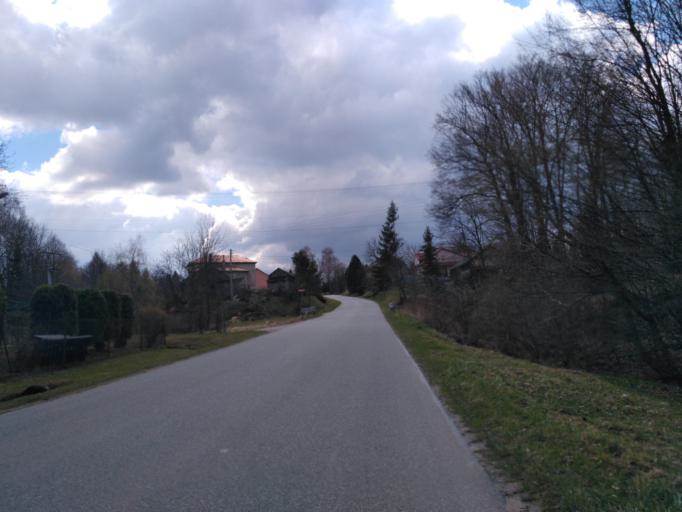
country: PL
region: Subcarpathian Voivodeship
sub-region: Powiat brzozowski
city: Dydnia
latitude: 49.6578
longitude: 22.2004
